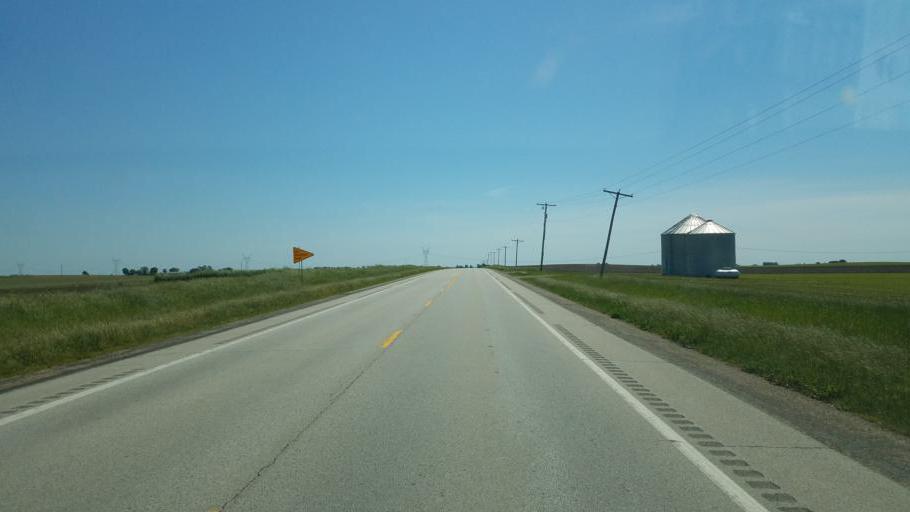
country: US
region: Illinois
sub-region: McLean County
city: Heyworth
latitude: 40.3123
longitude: -88.9449
